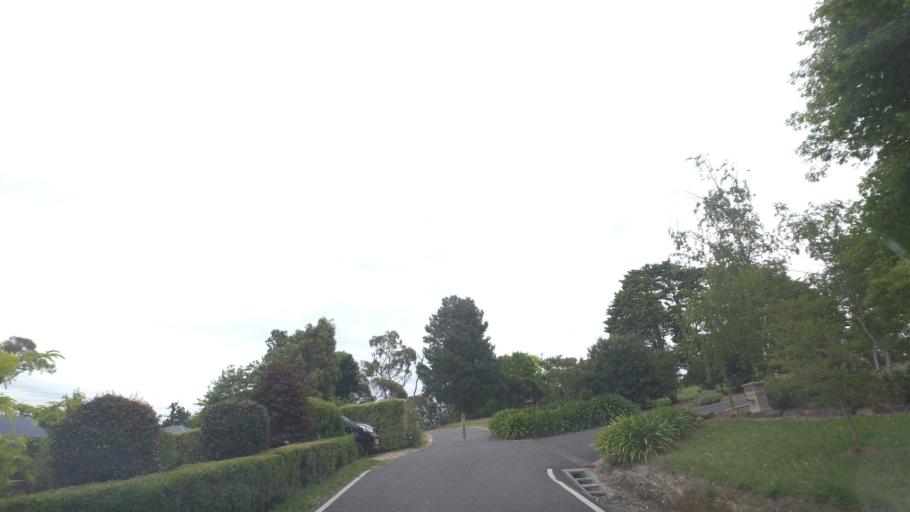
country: AU
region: Victoria
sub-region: Maroondah
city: Croydon North
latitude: -37.7906
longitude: 145.2943
